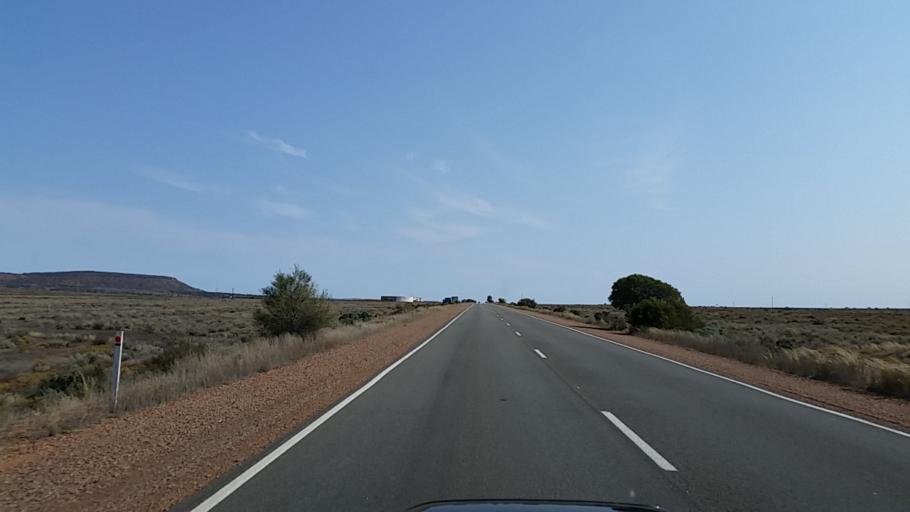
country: AU
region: South Australia
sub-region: Port Augusta
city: Port Augusta West
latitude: -32.6071
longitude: 137.5860
